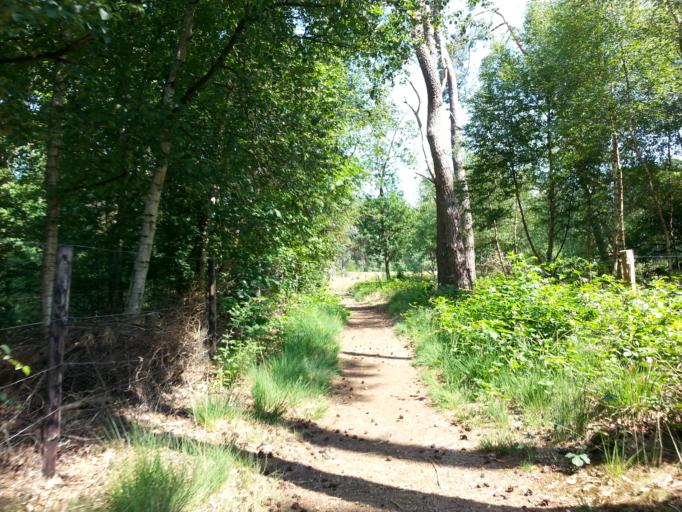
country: NL
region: Utrecht
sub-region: Gemeente Amersfoort
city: Amersfoort
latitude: 52.1142
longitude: 5.3757
